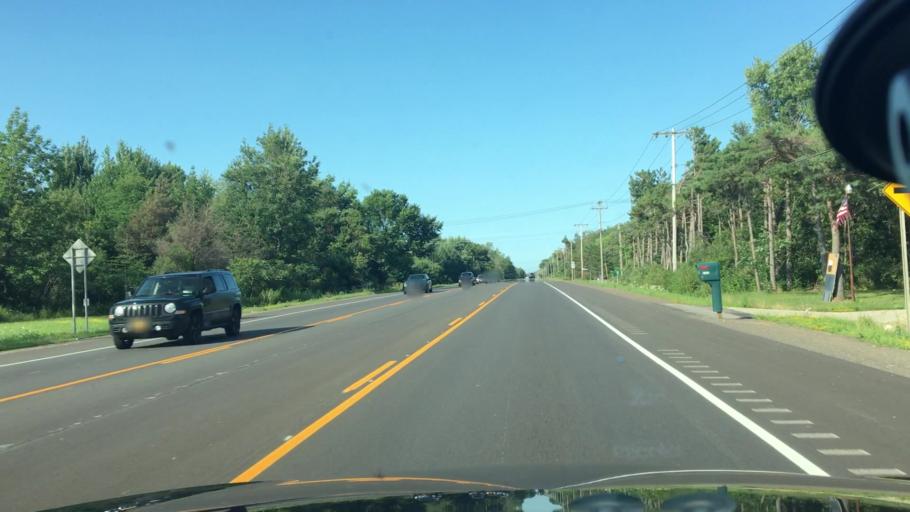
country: US
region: New York
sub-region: Erie County
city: Wanakah
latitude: 42.7113
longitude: -78.9136
